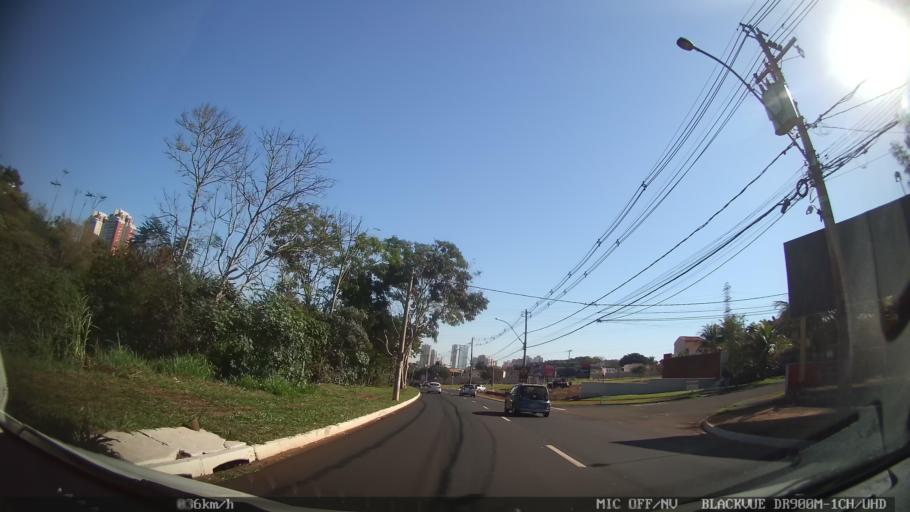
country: BR
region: Sao Paulo
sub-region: Ribeirao Preto
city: Ribeirao Preto
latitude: -21.2194
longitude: -47.7904
